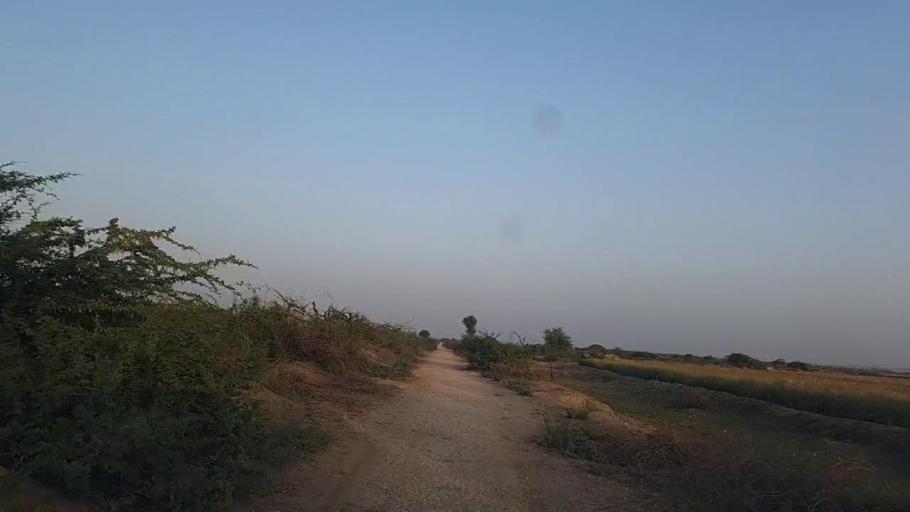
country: PK
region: Sindh
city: Naukot
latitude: 24.6973
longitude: 69.2623
